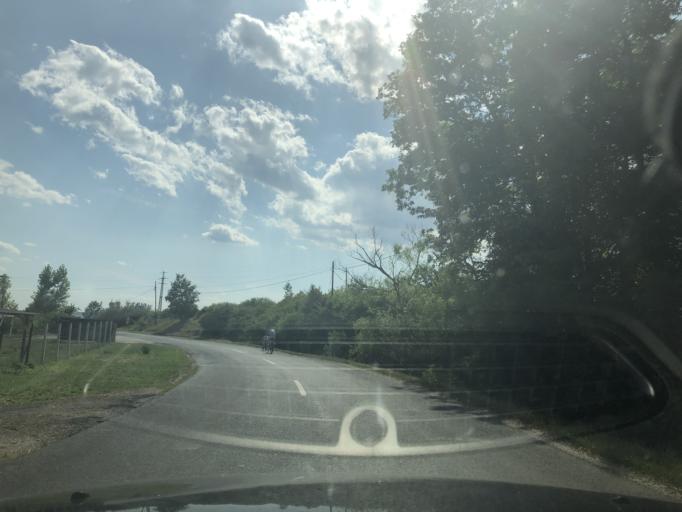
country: HU
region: Borsod-Abauj-Zemplen
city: Szendro
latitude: 48.4510
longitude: 20.7597
